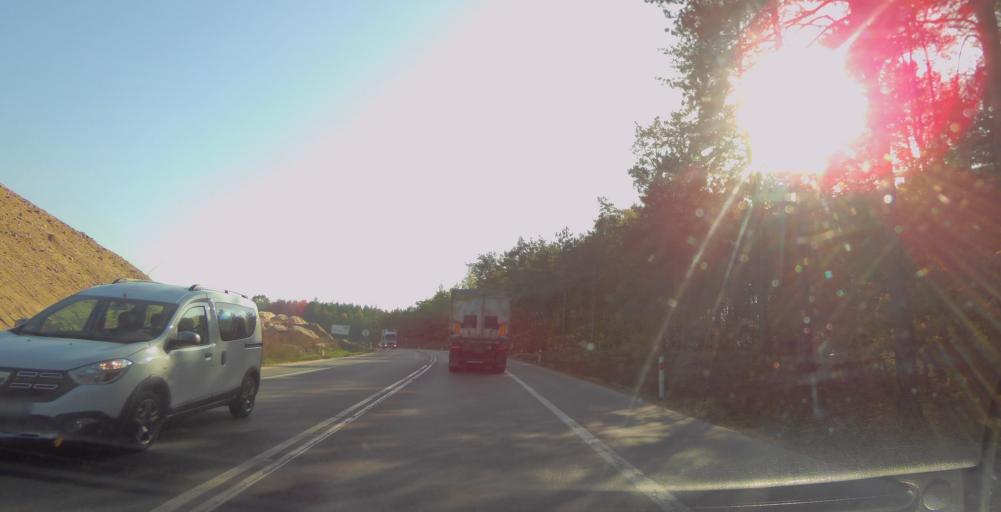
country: PL
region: Masovian Voivodeship
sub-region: Powiat otwocki
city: Jozefow
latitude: 52.1721
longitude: 21.2858
